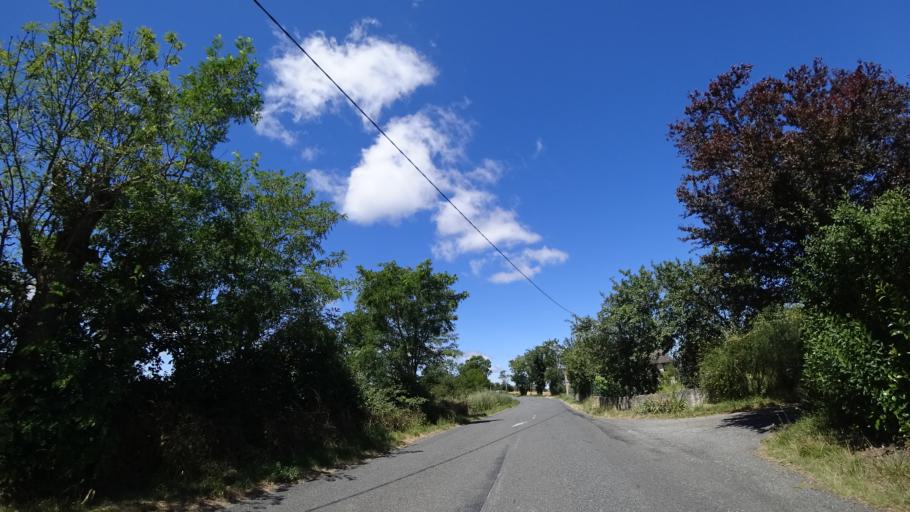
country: FR
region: Midi-Pyrenees
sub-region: Departement de l'Aveyron
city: Druelle
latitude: 44.3871
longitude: 2.5146
